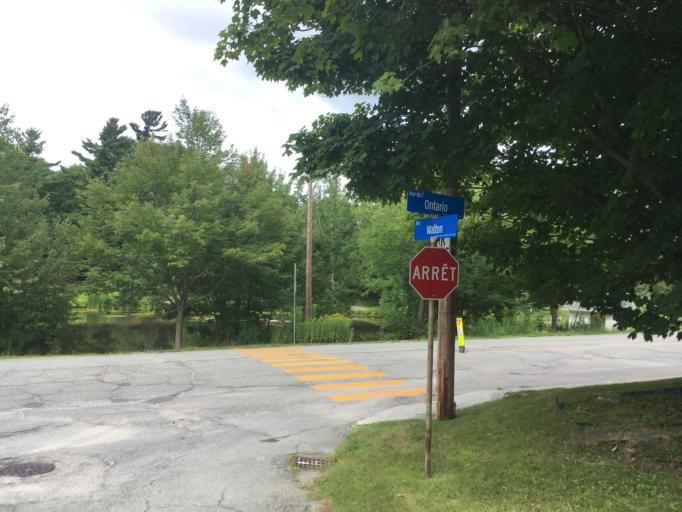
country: CA
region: Quebec
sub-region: Estrie
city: Sherbrooke
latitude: 45.4016
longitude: -71.9077
